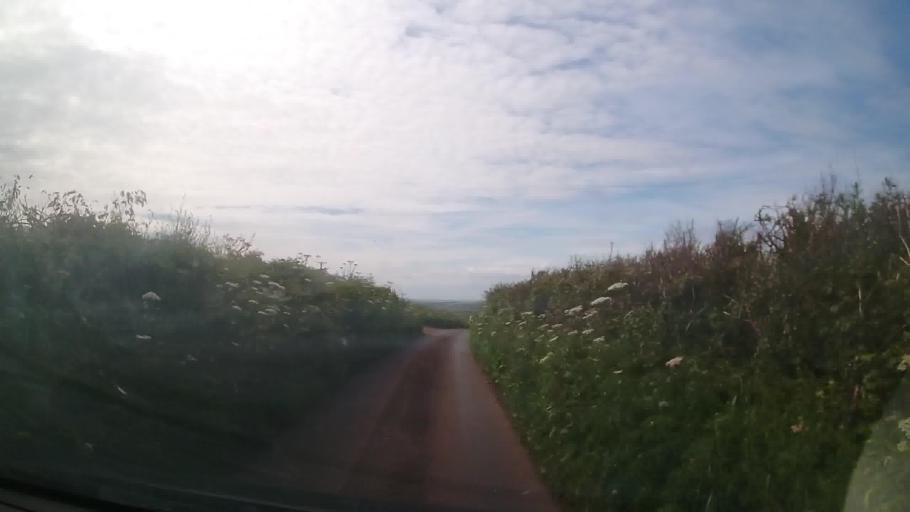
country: GB
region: England
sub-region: Devon
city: Salcombe
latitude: 50.2300
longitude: -3.6673
